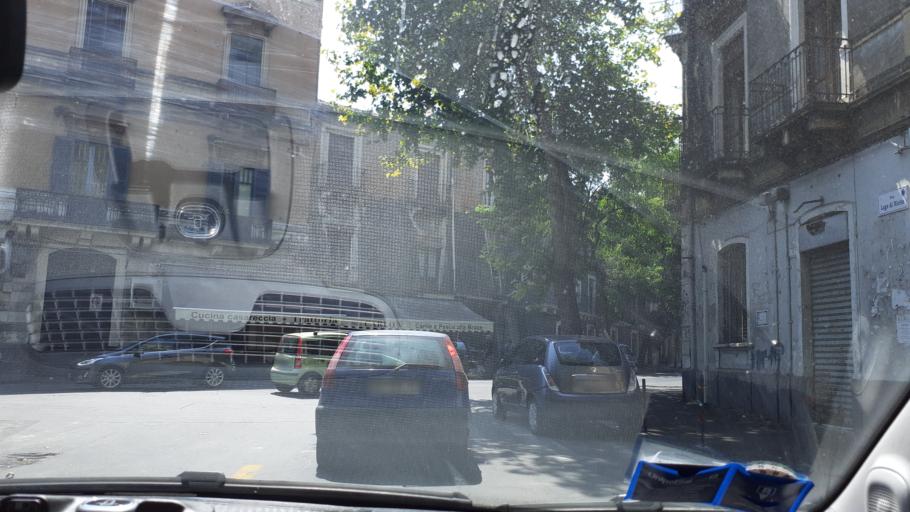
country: IT
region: Sicily
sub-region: Catania
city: Catania
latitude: 37.5076
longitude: 15.0794
